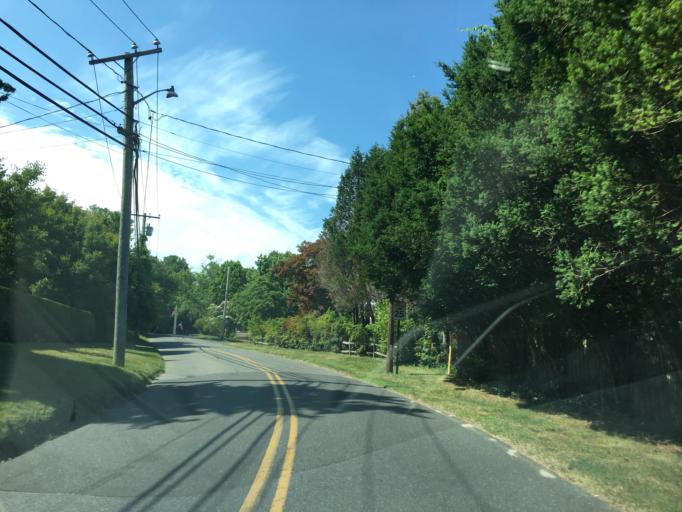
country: US
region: New York
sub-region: Suffolk County
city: Shelter Island Heights
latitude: 41.0808
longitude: -72.3547
